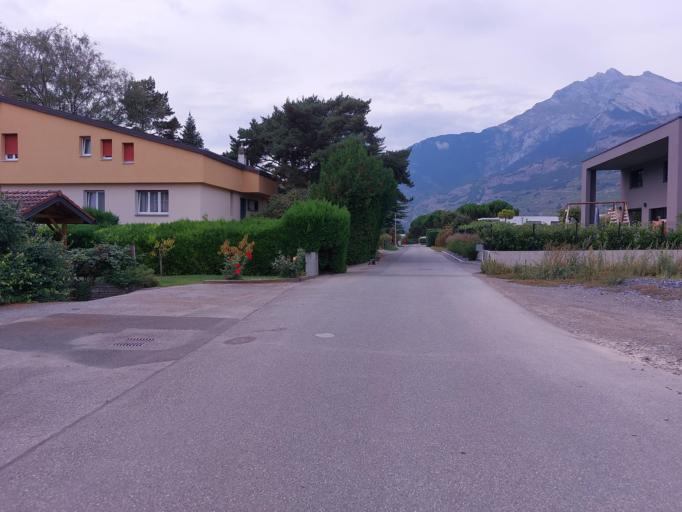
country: CH
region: Valais
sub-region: Conthey District
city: Conthey
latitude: 46.2270
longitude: 7.3080
